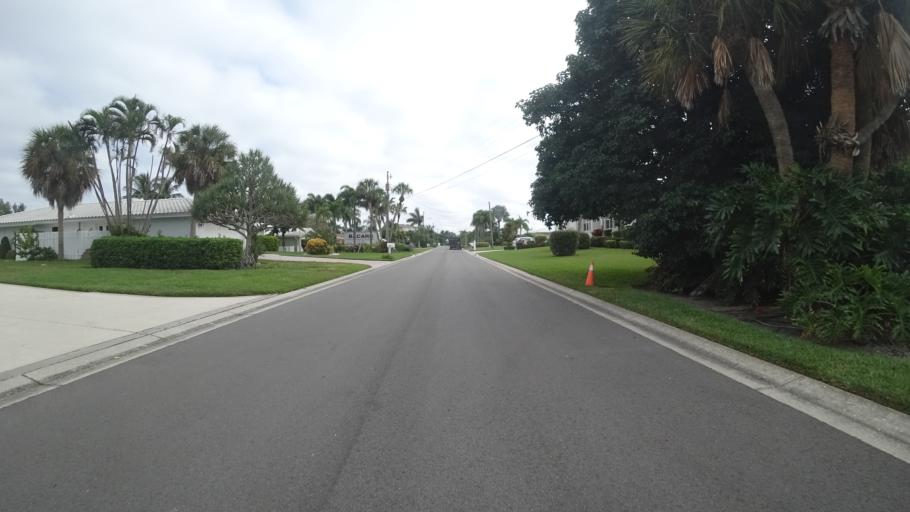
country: US
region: Florida
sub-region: Manatee County
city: Longboat Key
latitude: 27.4217
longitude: -82.6649
